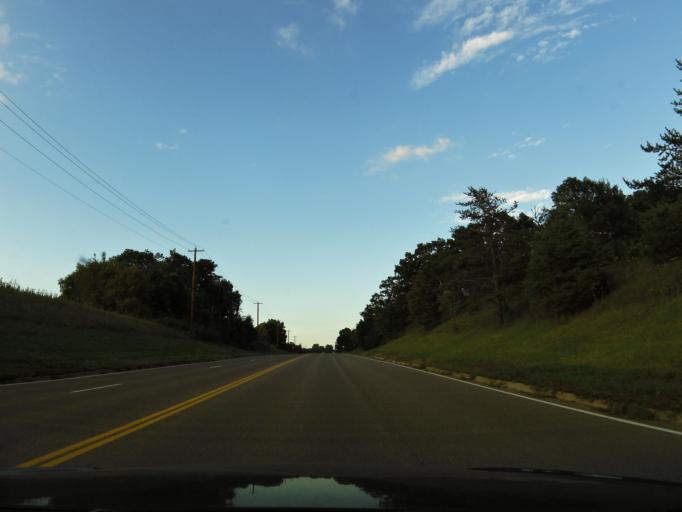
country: US
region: Minnesota
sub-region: Washington County
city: Cottage Grove
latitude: 44.8091
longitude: -92.9093
